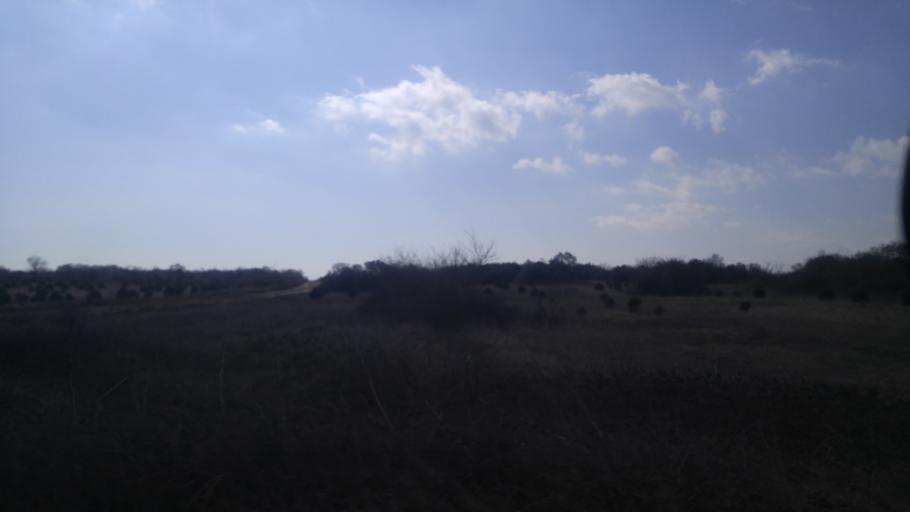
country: TR
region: Istanbul
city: Canta
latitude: 41.1709
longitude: 28.0944
